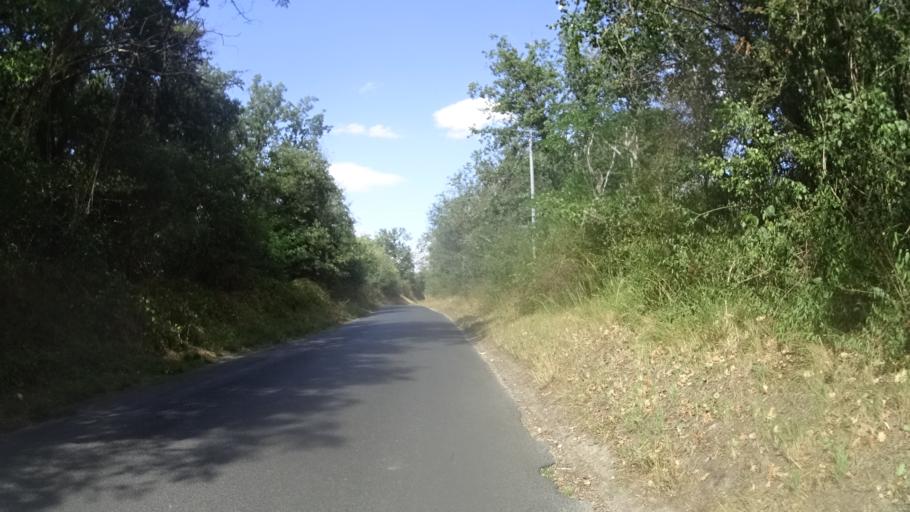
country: FR
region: Ile-de-France
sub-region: Departement de l'Essonne
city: Maisse
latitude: 48.3838
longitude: 2.3898
